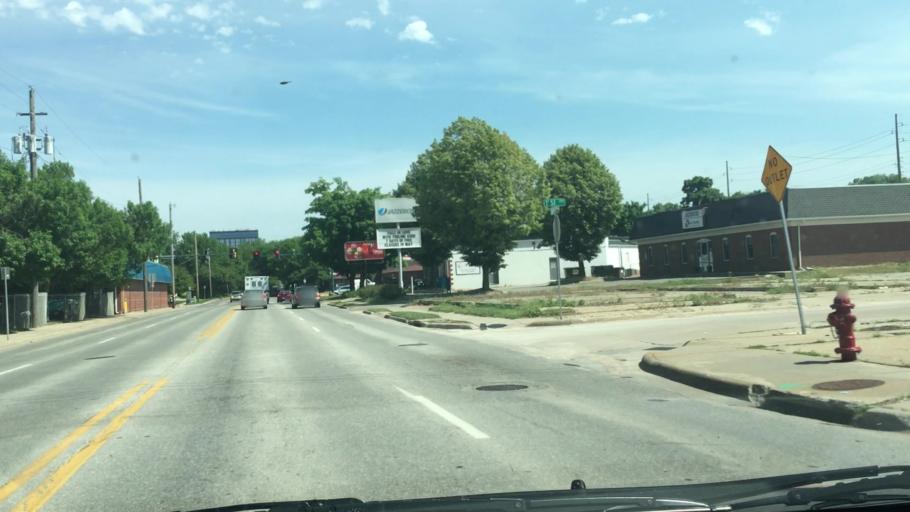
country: US
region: Iowa
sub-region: Johnson County
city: Iowa City
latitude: 41.6483
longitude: -91.5320
